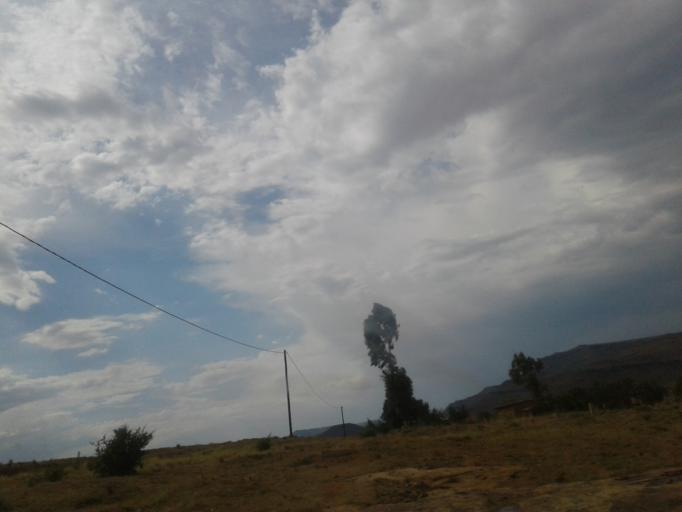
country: LS
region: Quthing
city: Quthing
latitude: -30.3758
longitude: 27.5555
